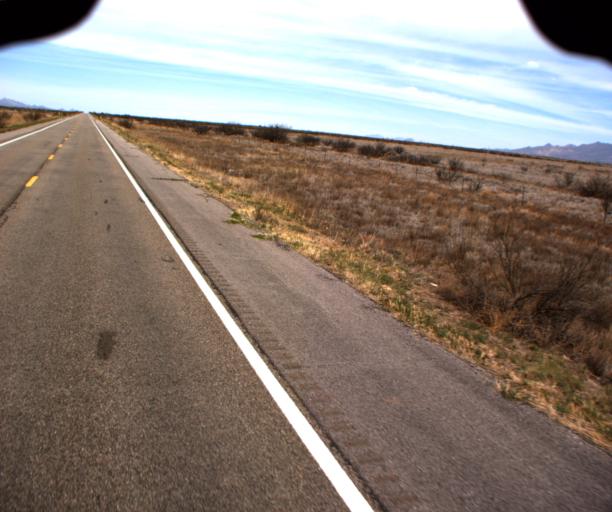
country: US
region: Arizona
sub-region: Cochise County
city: Pirtleville
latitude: 31.4964
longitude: -109.6329
